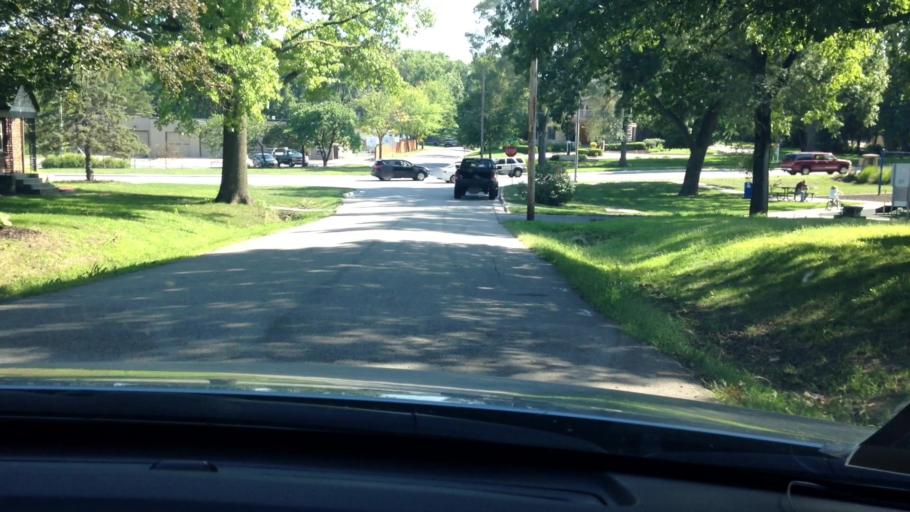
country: US
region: Kansas
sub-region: Johnson County
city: Shawnee
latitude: 39.0228
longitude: -94.7292
